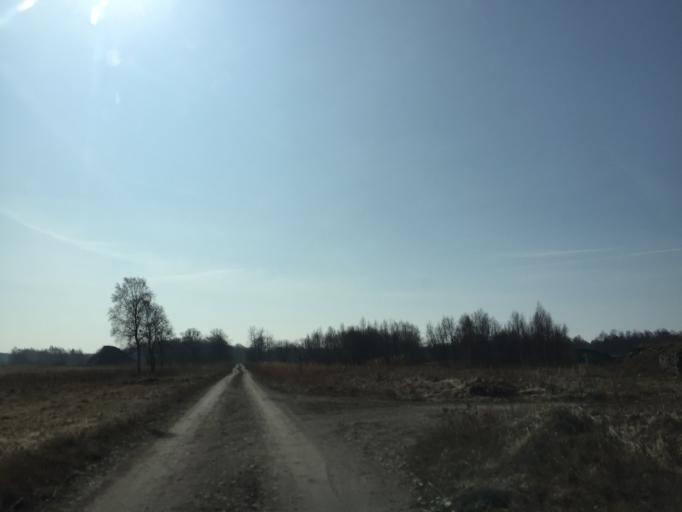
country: LV
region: Dundaga
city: Dundaga
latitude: 57.9295
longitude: 22.0632
